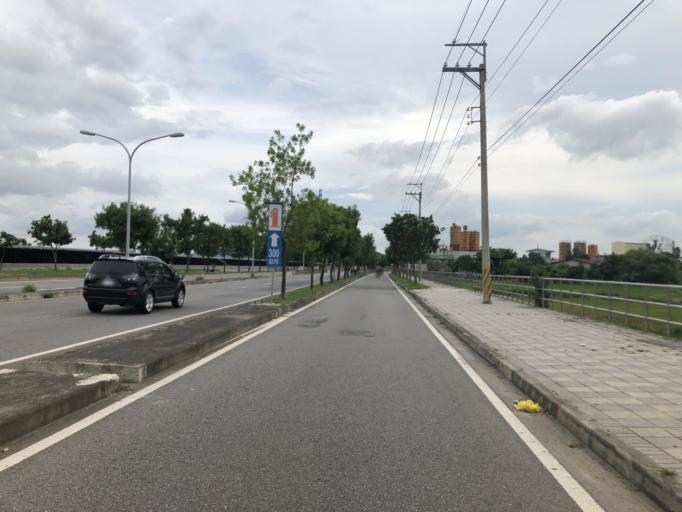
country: TW
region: Taiwan
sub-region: Taichung City
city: Taichung
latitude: 24.0886
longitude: 120.6810
